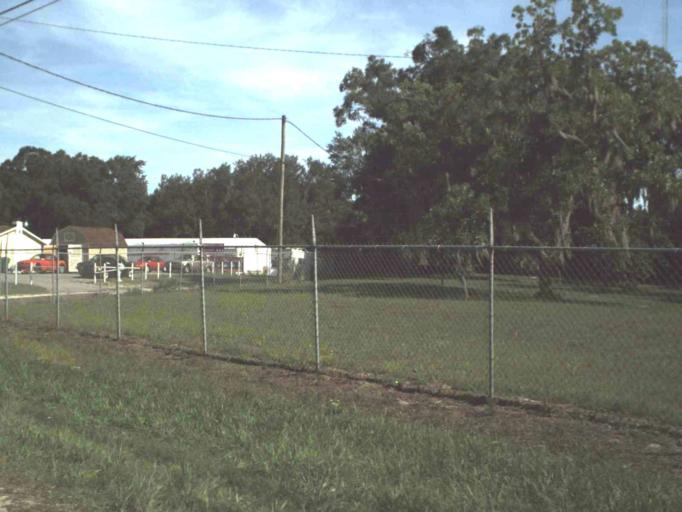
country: US
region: Florida
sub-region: Volusia County
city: DeLand
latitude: 29.0272
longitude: -81.2700
